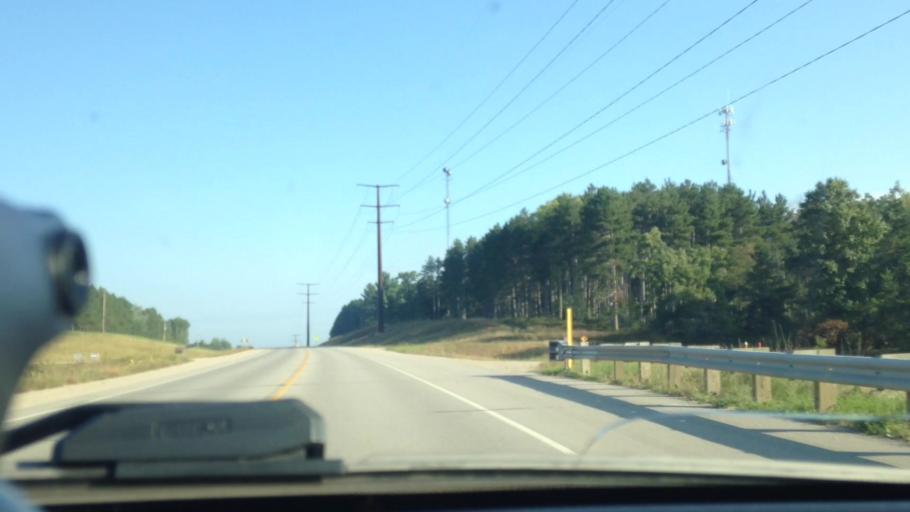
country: US
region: Wisconsin
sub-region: Marinette County
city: Peshtigo
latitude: 45.2105
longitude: -87.9948
